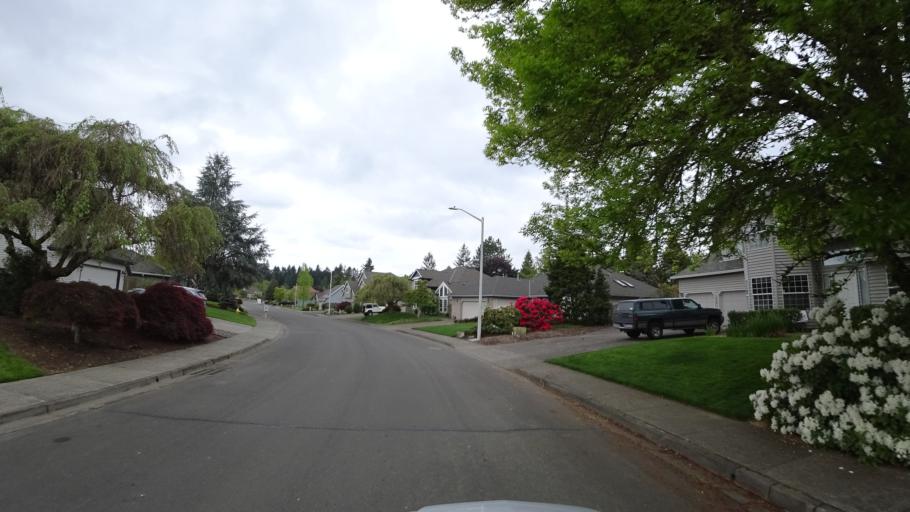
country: US
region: Oregon
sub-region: Washington County
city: Hillsboro
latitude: 45.5385
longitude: -122.9816
